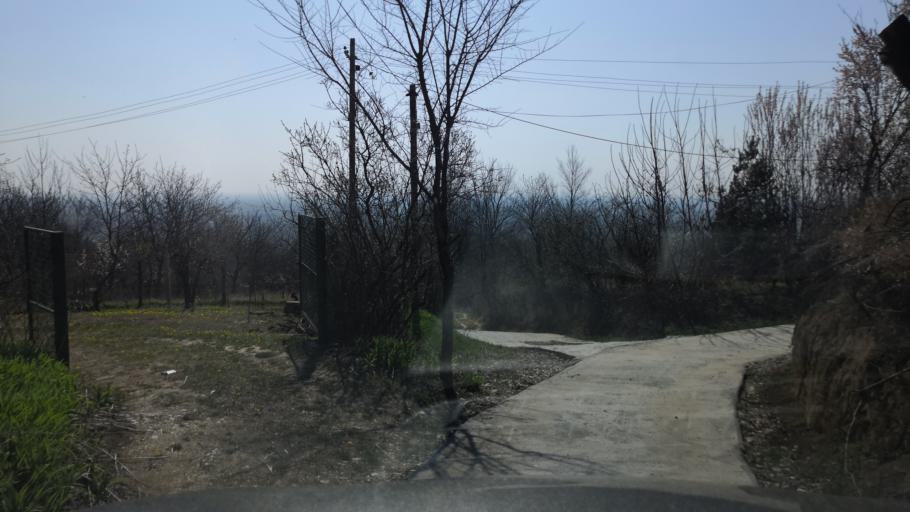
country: RS
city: Krcedin
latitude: 45.1604
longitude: 20.1865
